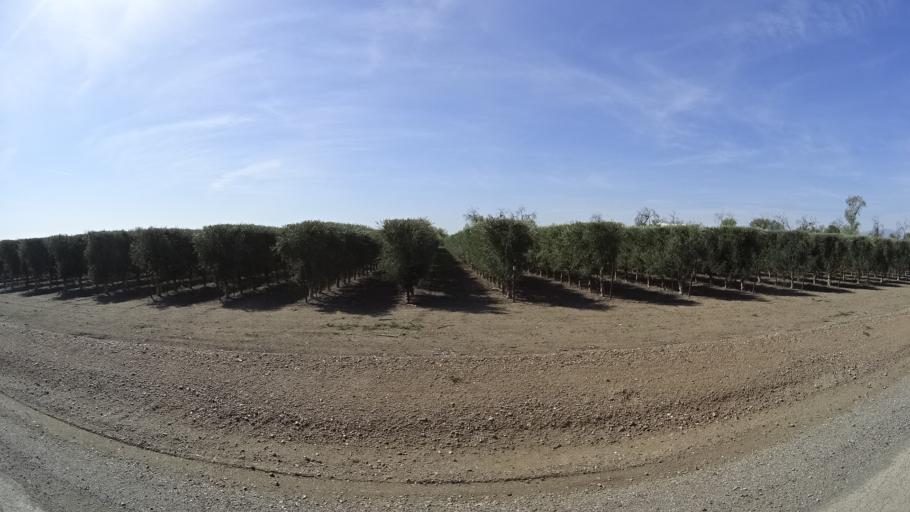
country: US
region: California
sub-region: Glenn County
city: Willows
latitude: 39.6117
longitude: -122.2577
